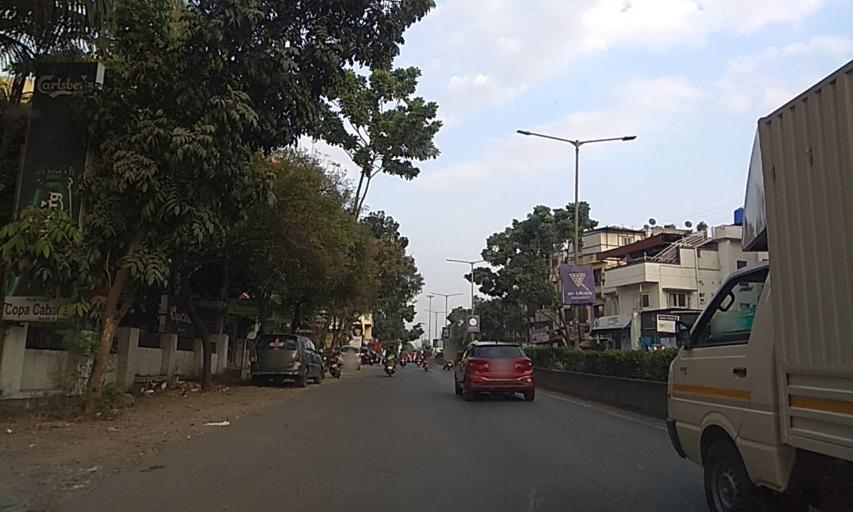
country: IN
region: Maharashtra
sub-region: Pune Division
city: Pimpri
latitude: 18.5885
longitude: 73.7824
